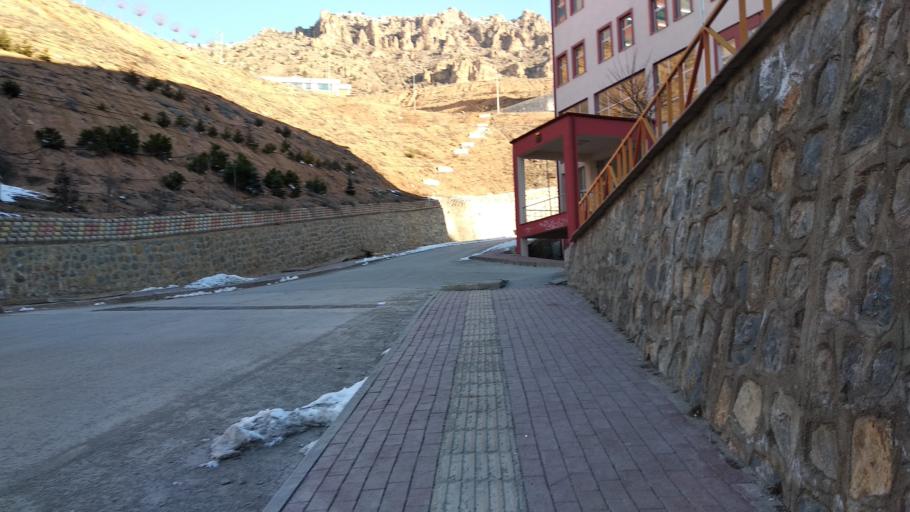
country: TR
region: Gumushane
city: Gumushkhane
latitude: 40.4379
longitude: 39.5160
